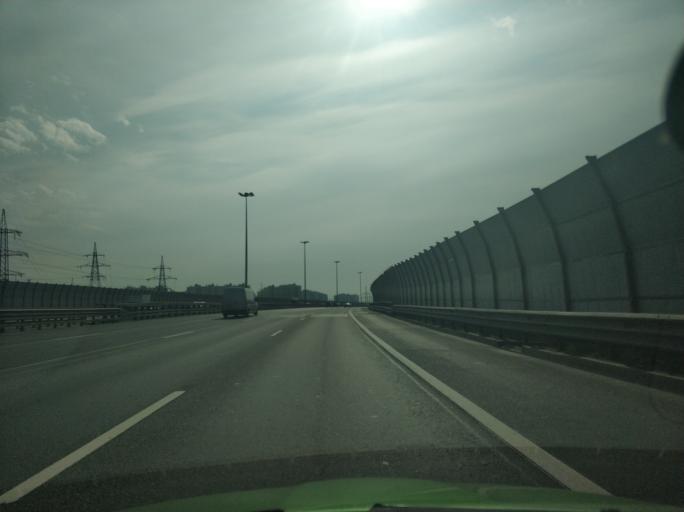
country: RU
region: Leningrad
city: Murino
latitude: 60.0424
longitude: 30.4369
